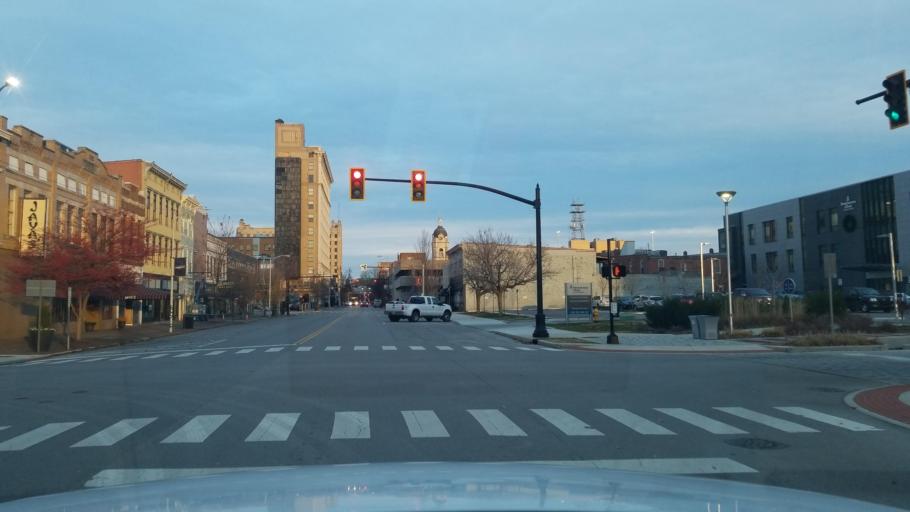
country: US
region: Indiana
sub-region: Vanderburgh County
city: Evansville
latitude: 37.9698
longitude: -87.5697
